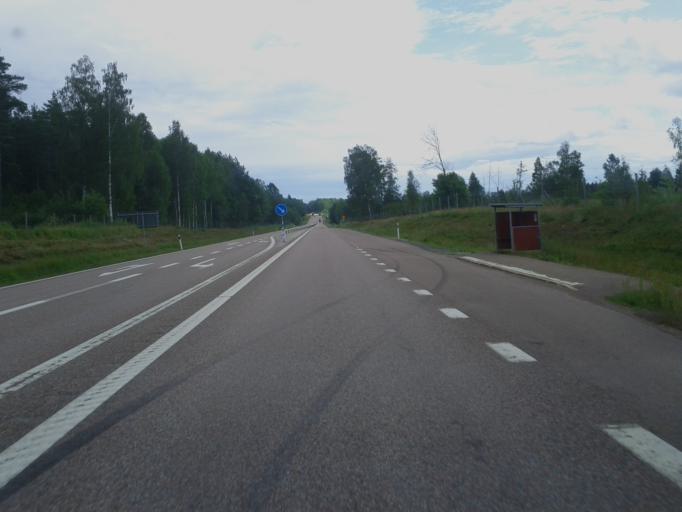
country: SE
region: Dalarna
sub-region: Saters Kommun
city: Saeter
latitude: 60.3288
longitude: 15.8447
